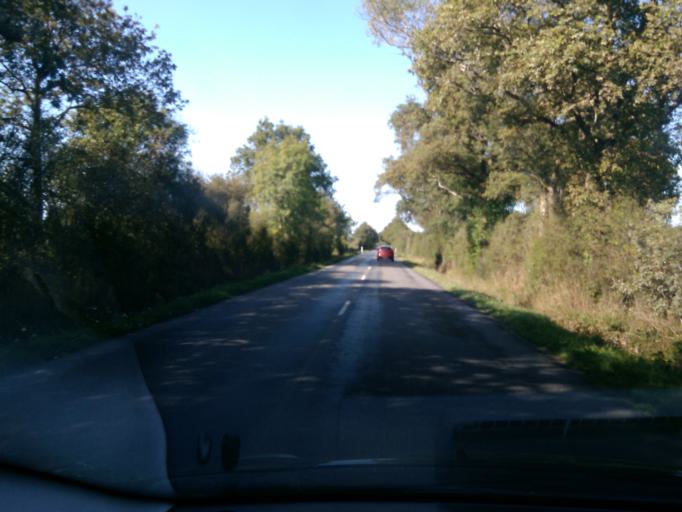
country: FR
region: Pays de la Loire
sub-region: Departement de la Loire-Atlantique
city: Quilly
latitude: 47.4281
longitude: -1.9275
